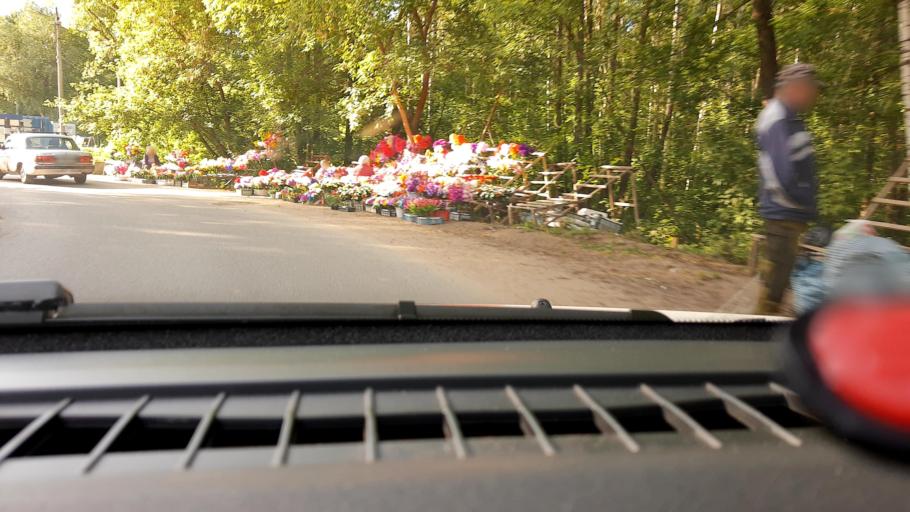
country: RU
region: Nizjnij Novgorod
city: Gorbatovka
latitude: 56.2310
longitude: 43.7630
